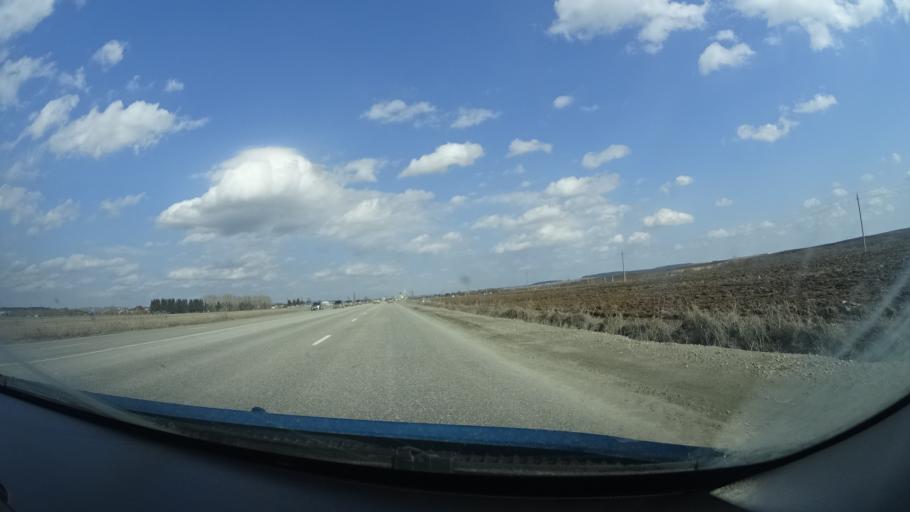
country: RU
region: Perm
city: Kultayevo
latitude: 57.8812
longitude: 55.9157
